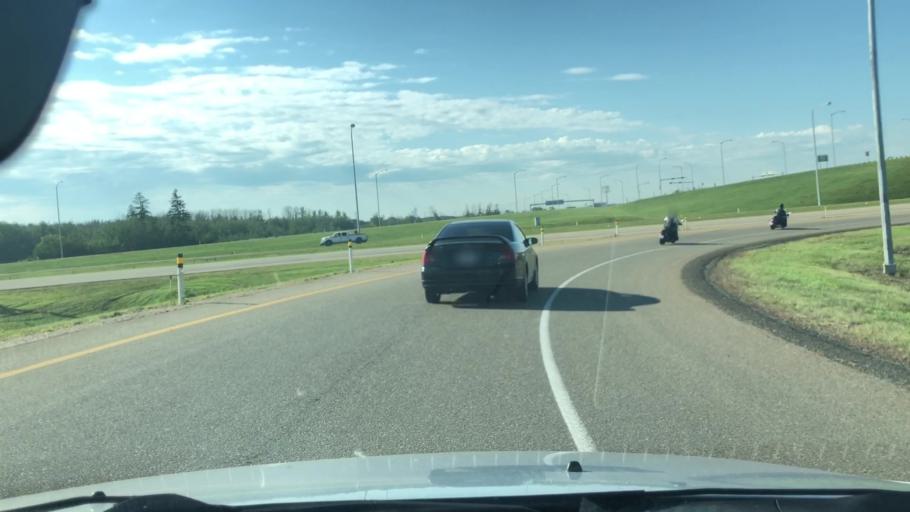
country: CA
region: Alberta
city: St. Albert
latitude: 53.6405
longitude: -113.5442
